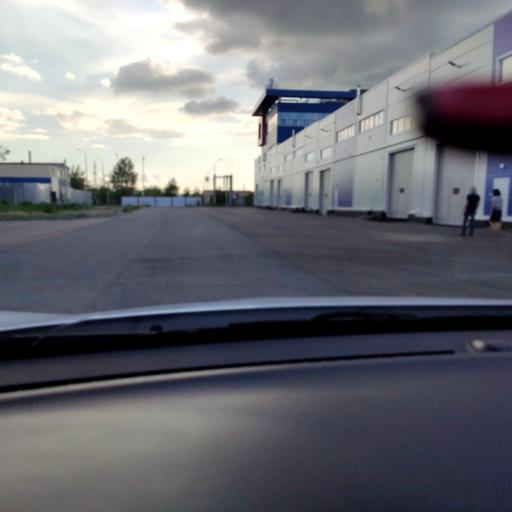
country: RU
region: Tatarstan
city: Staroye Arakchino
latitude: 55.8295
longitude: 49.0358
